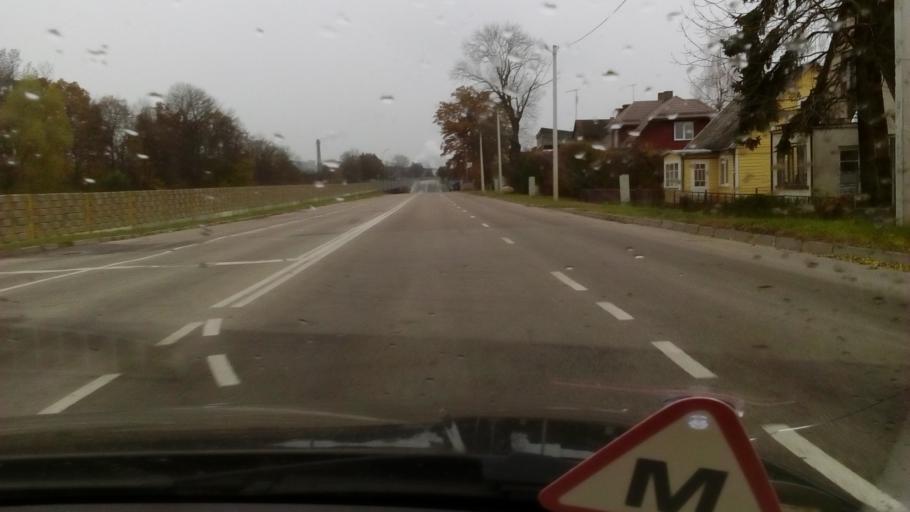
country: LT
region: Marijampoles apskritis
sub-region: Marijampole Municipality
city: Marijampole
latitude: 54.5475
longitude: 23.3577
